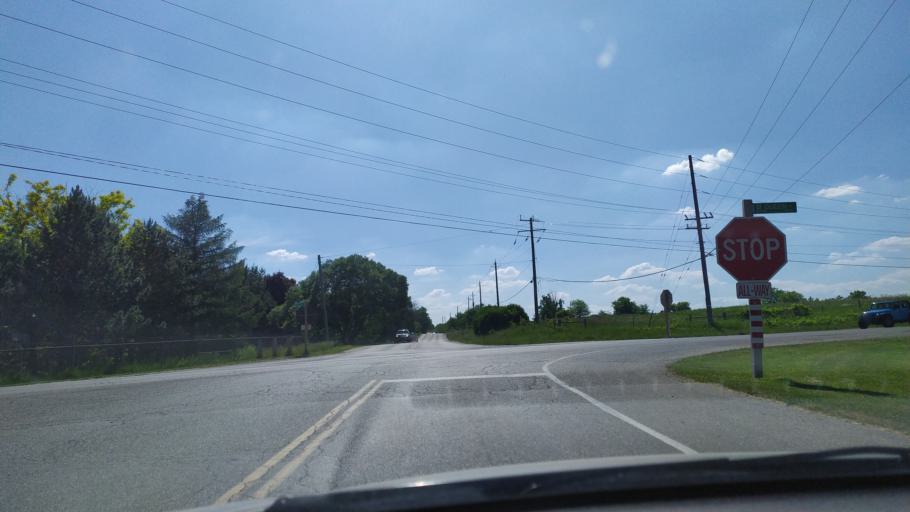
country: CA
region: Ontario
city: Kitchener
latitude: 43.3714
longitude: -80.5592
